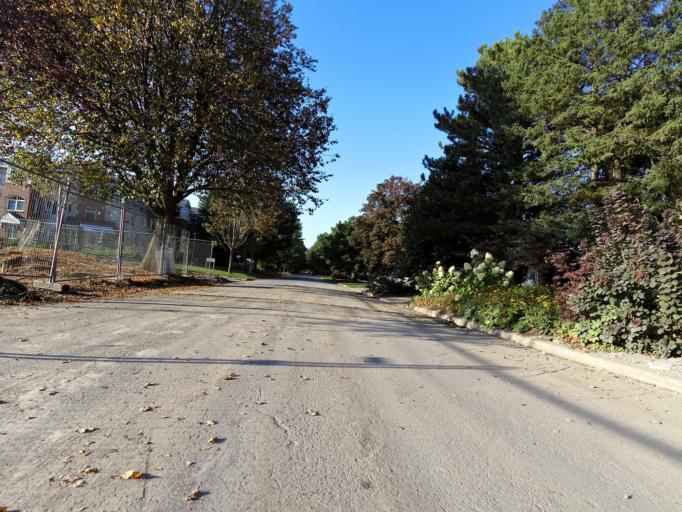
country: CA
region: Ontario
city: Ottawa
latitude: 45.3836
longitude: -75.6602
